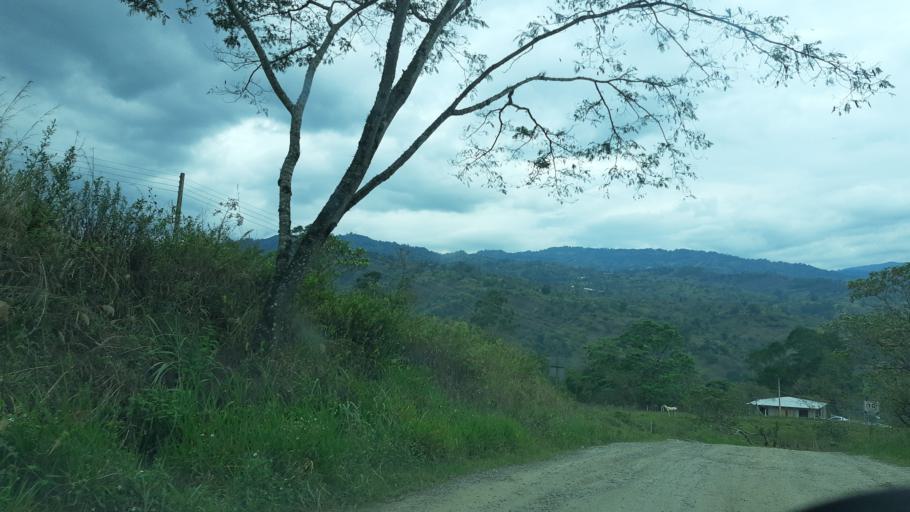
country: CO
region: Boyaca
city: Garagoa
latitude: 5.0670
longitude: -73.3830
